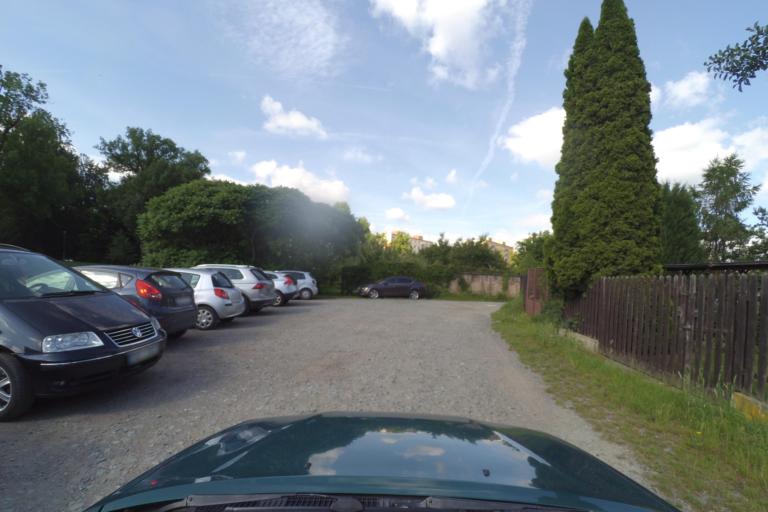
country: CZ
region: Kralovehradecky
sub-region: Okres Nachod
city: Jaromer
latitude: 50.3548
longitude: 15.9187
